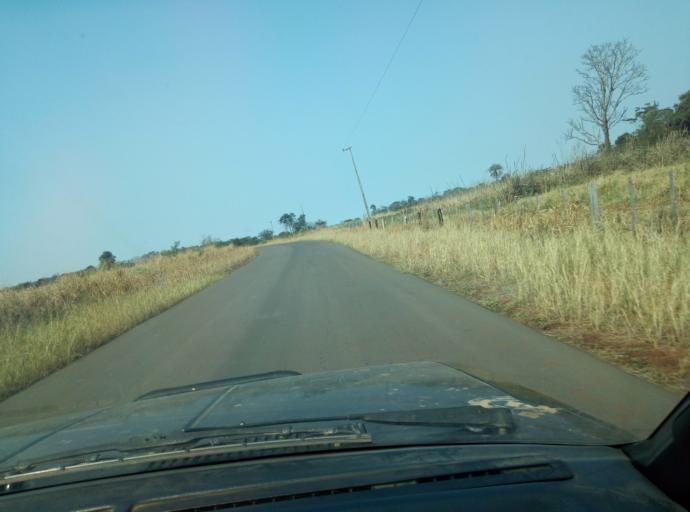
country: PY
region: Caaguazu
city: Carayao
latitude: -25.2300
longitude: -56.2892
